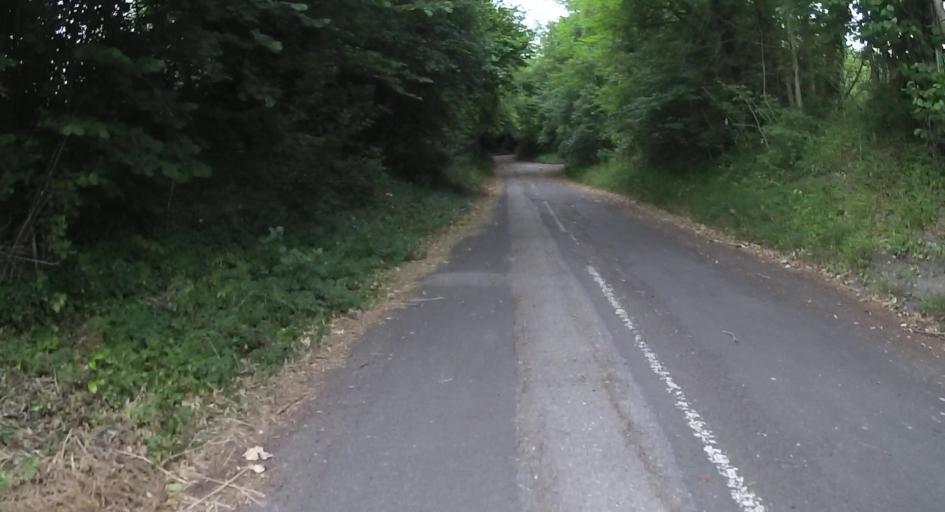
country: GB
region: England
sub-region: Surrey
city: Seale
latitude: 51.2236
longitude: -0.7336
